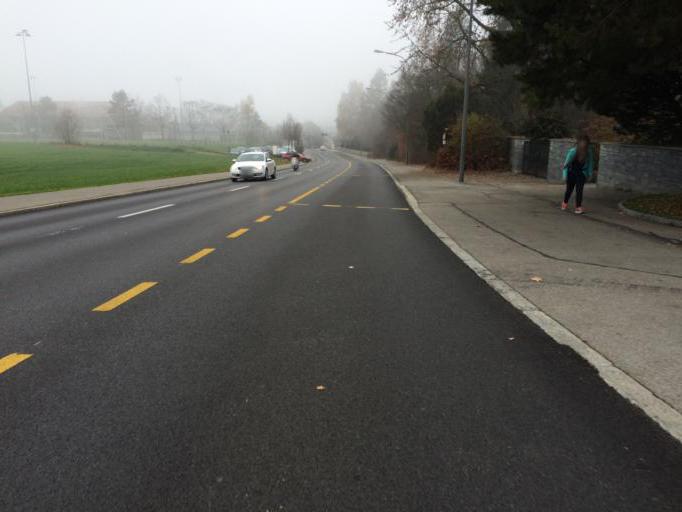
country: CH
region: Bern
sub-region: Bern-Mittelland District
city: Koniz
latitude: 46.9193
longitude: 7.4170
